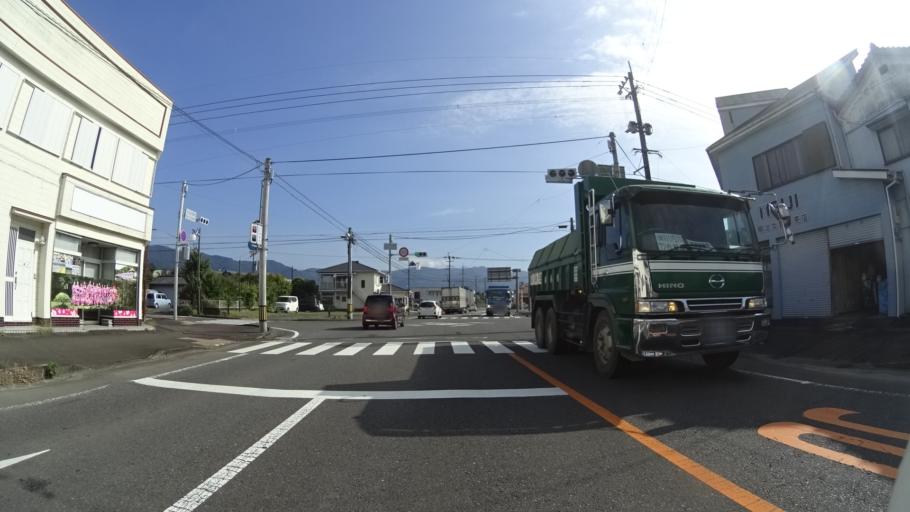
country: JP
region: Kagoshima
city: Okuchi-shinohara
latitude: 32.0465
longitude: 130.7651
